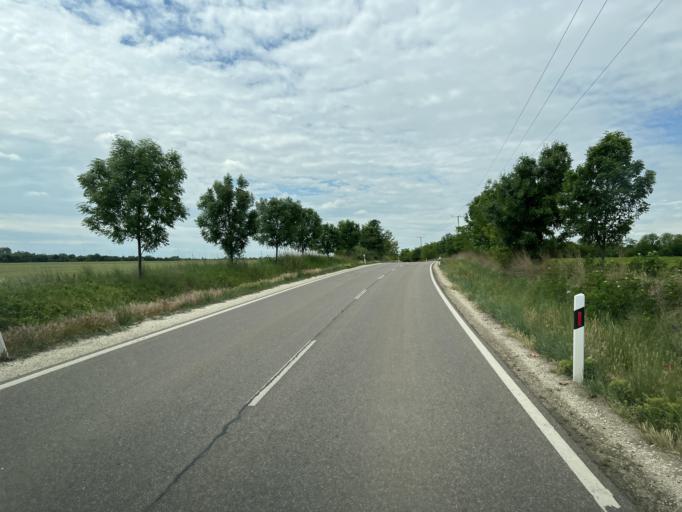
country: HU
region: Pest
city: Koka
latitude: 47.5022
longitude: 19.5904
